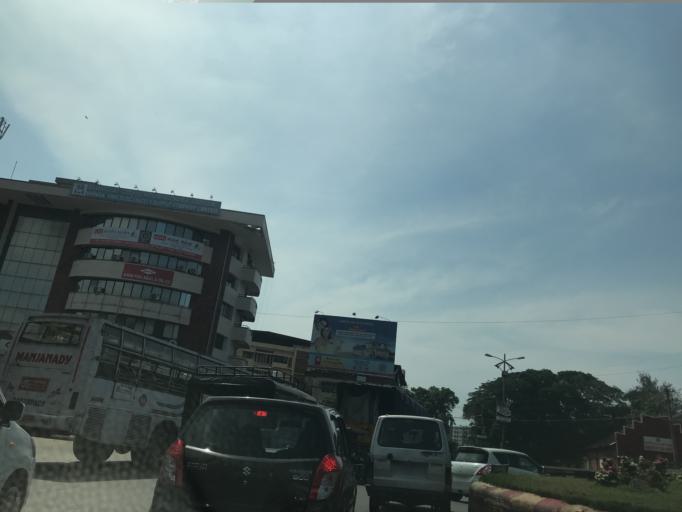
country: IN
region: Karnataka
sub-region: Dakshina Kannada
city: Ullal
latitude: 12.8610
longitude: 74.8391
